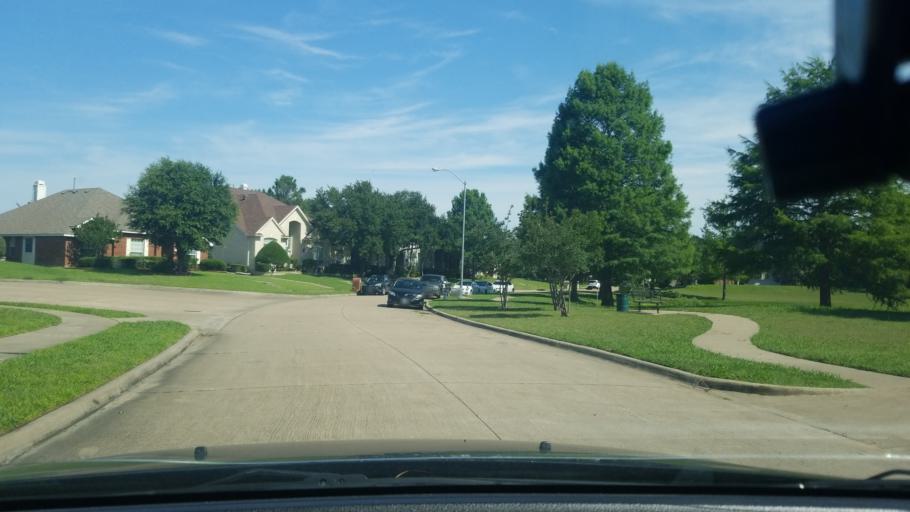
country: US
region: Texas
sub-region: Dallas County
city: Mesquite
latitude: 32.7774
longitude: -96.5828
